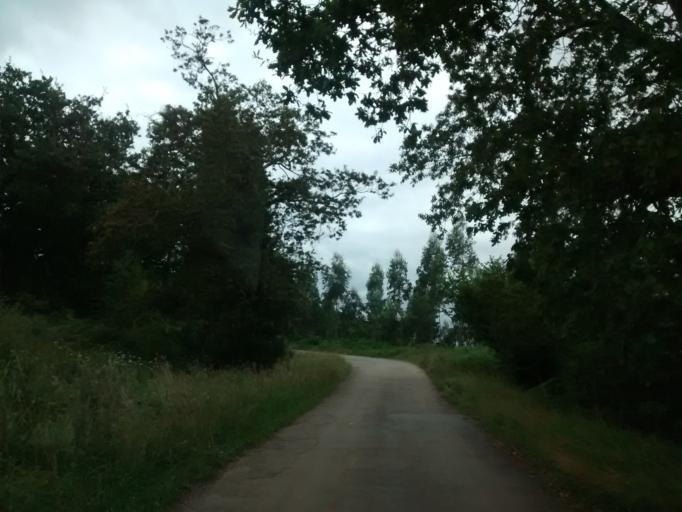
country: ES
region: Cantabria
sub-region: Provincia de Cantabria
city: Comillas
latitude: 43.3425
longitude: -4.2937
